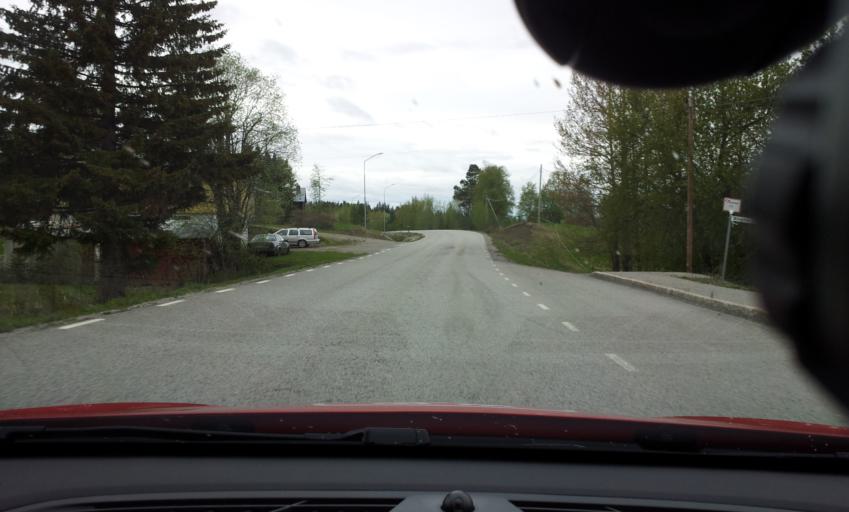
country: SE
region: Jaemtland
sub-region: Bergs Kommun
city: Hoverberg
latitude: 62.7632
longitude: 14.5578
